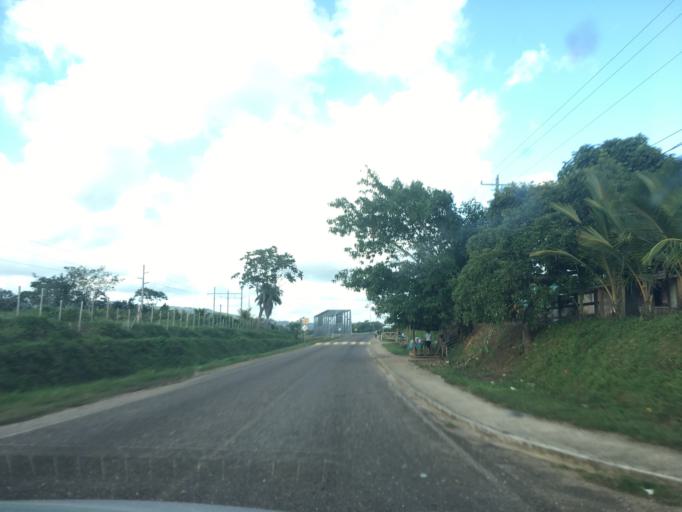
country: BZ
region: Stann Creek
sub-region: Dangriga
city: Dangriga
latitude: 16.8126
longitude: -88.3786
